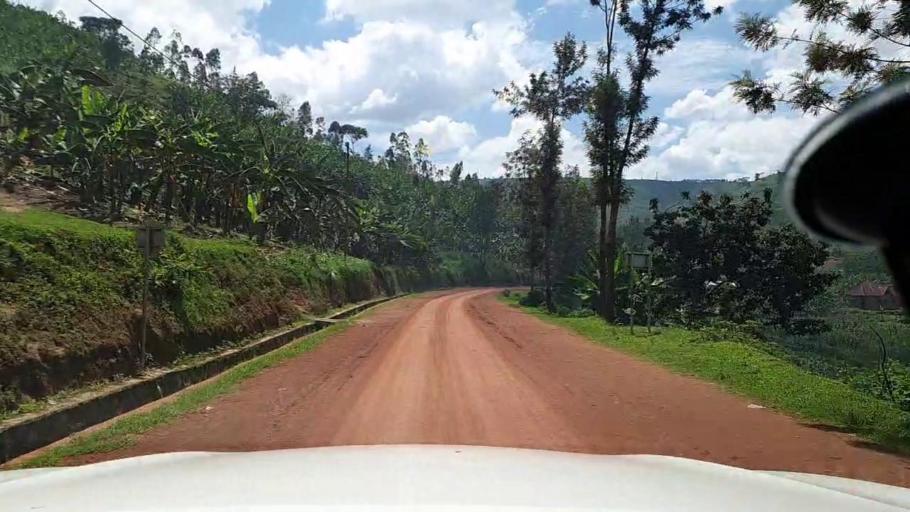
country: RW
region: Northern Province
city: Musanze
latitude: -1.6918
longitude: 29.8215
